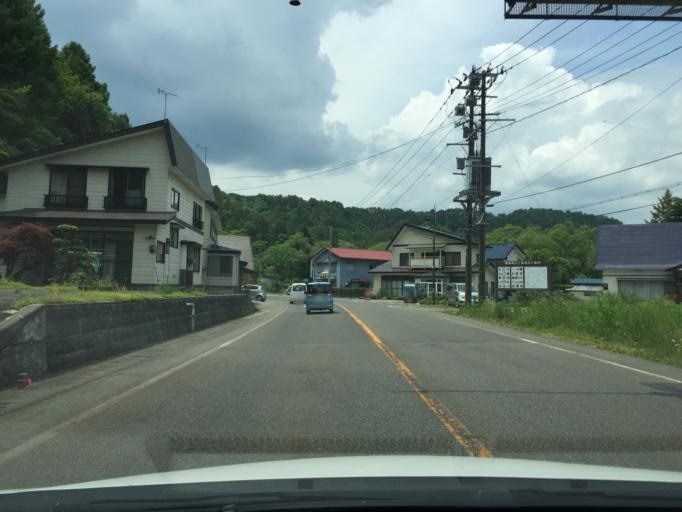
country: JP
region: Fukushima
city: Inawashiro
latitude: 37.6375
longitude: 140.1018
